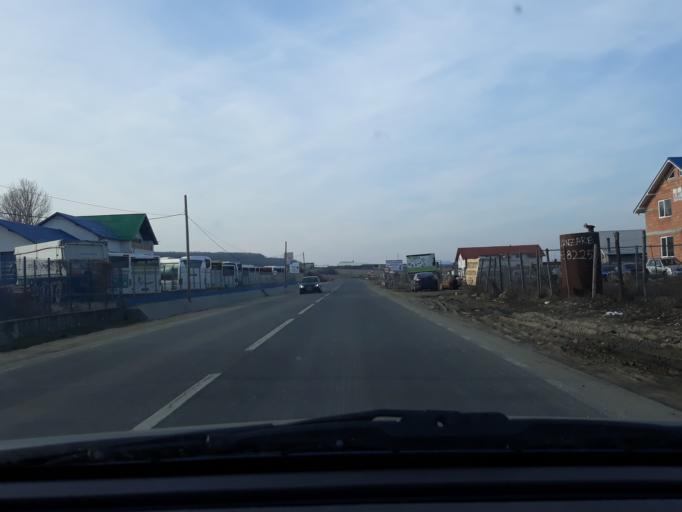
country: RO
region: Salaj
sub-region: Comuna Hereclean
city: Hereclean
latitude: 47.2280
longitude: 23.0027
